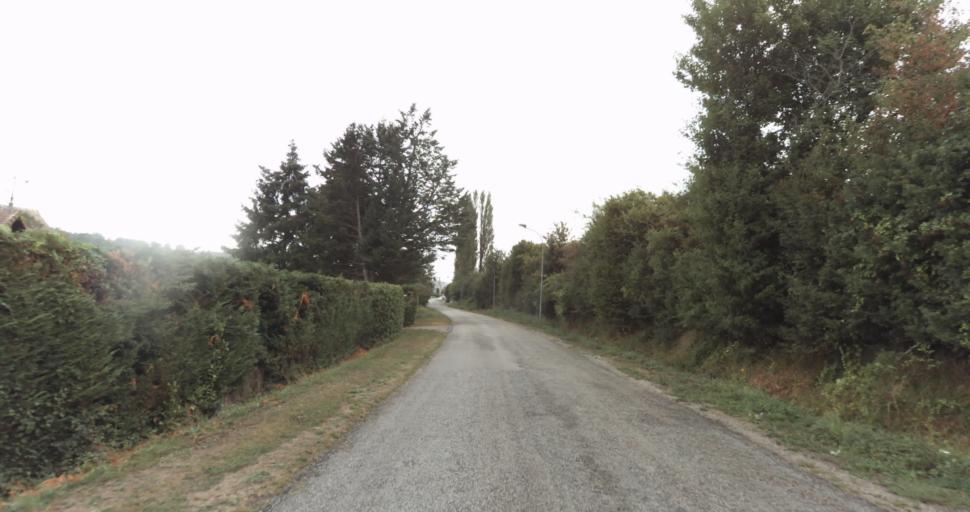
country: FR
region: Lower Normandy
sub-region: Departement de l'Orne
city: Vimoutiers
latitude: 48.9205
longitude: 0.2071
